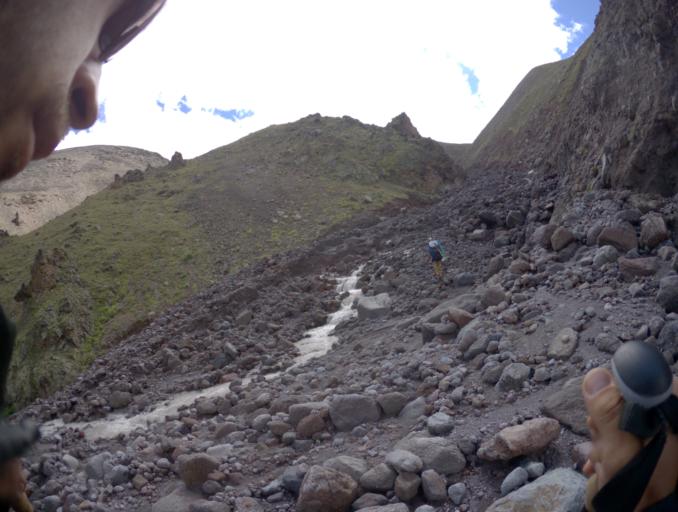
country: RU
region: Kabardino-Balkariya
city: Terskol
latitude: 43.3851
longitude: 42.3667
